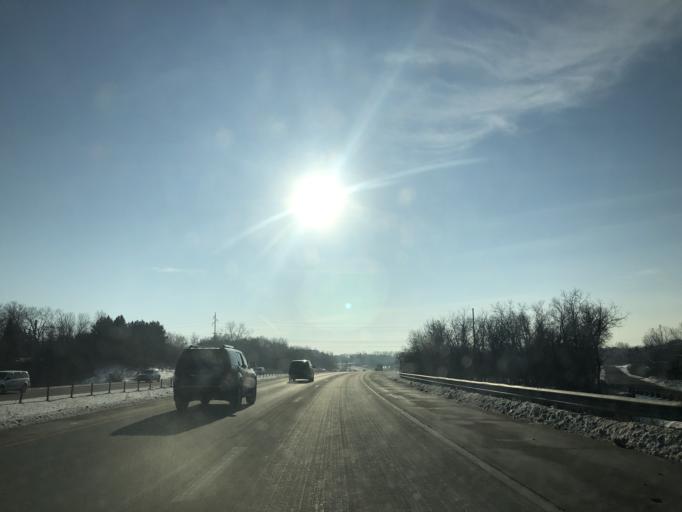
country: US
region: Minnesota
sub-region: Ramsey County
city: Shoreview
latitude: 45.0734
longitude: -93.1699
